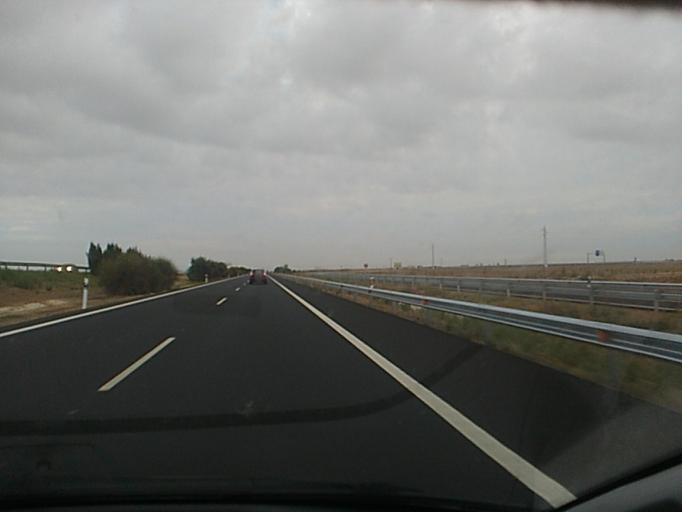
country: ES
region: Castille and Leon
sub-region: Provincia de Zamora
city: Castrogonzalo
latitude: 41.9681
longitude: -5.5947
